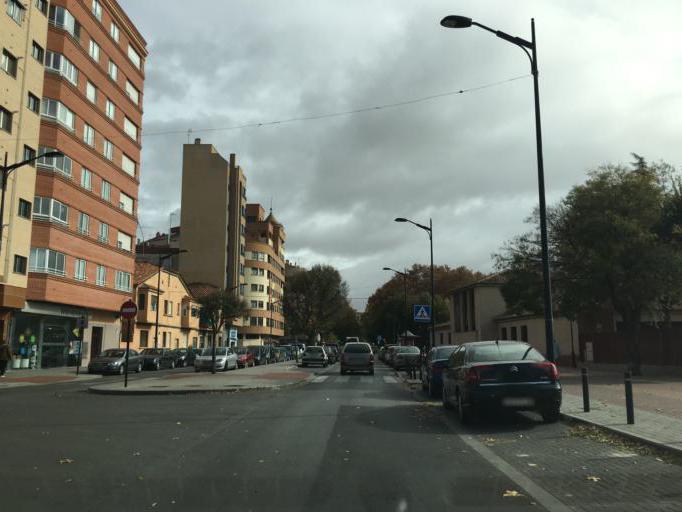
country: ES
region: Castille-La Mancha
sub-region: Provincia de Albacete
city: Albacete
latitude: 38.9980
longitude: -1.8683
